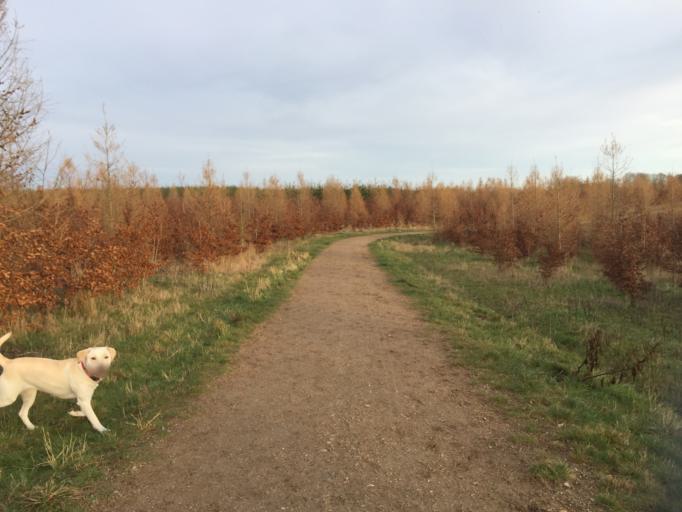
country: DK
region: South Denmark
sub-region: Odense Kommune
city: Bellinge
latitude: 55.3700
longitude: 10.3118
